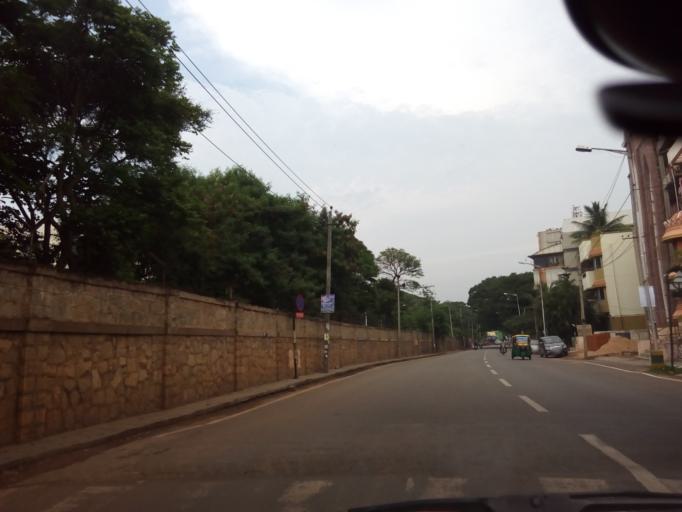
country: IN
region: Karnataka
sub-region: Bangalore Urban
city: Bangalore
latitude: 13.0243
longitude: 77.5627
